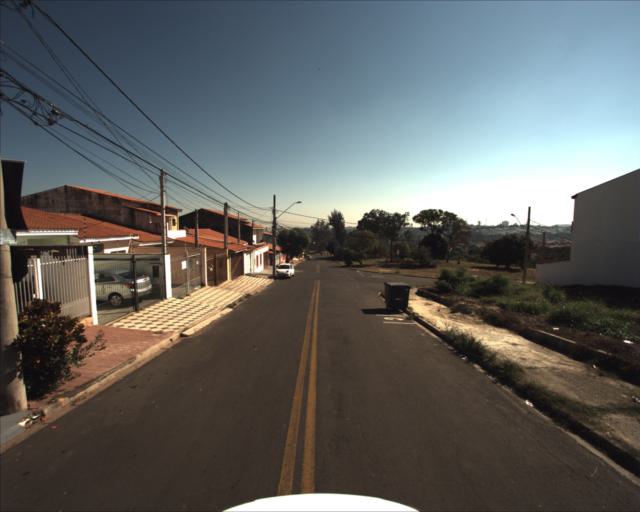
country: BR
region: Sao Paulo
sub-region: Sorocaba
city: Sorocaba
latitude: -23.4966
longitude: -47.4219
